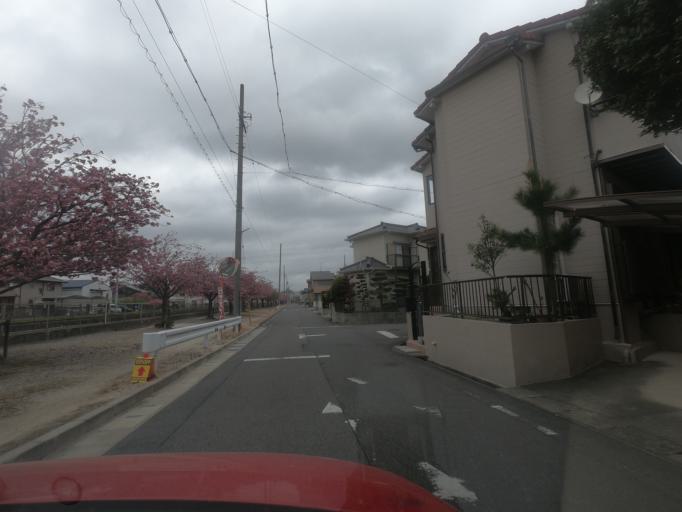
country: JP
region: Aichi
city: Kasugai
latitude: 35.2643
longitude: 136.9546
